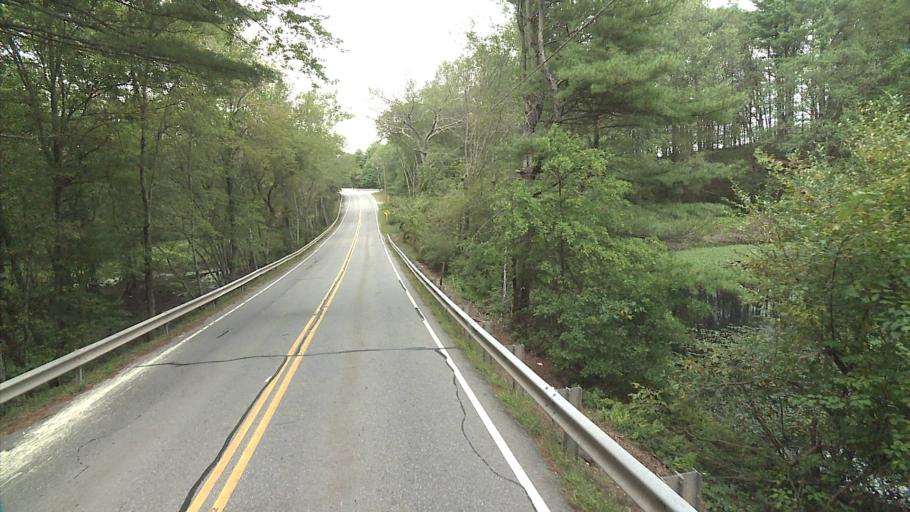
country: US
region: Connecticut
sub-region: New London County
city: Jewett City
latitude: 41.6485
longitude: -71.9634
